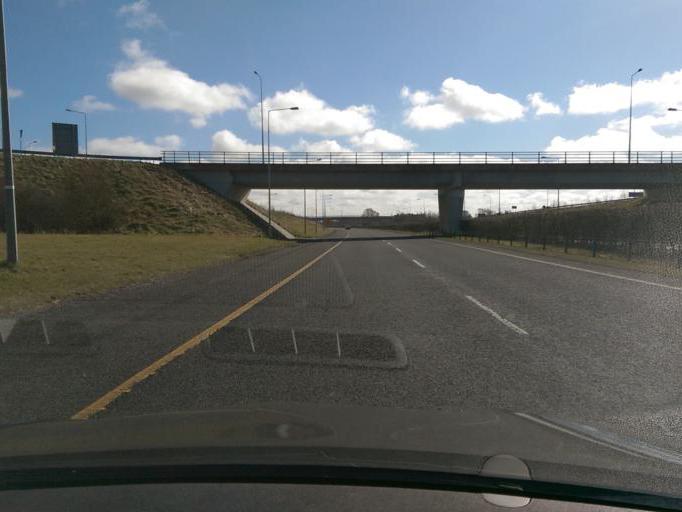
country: IE
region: Leinster
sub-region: An Mhi
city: Enfield
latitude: 53.4096
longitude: -6.8475
